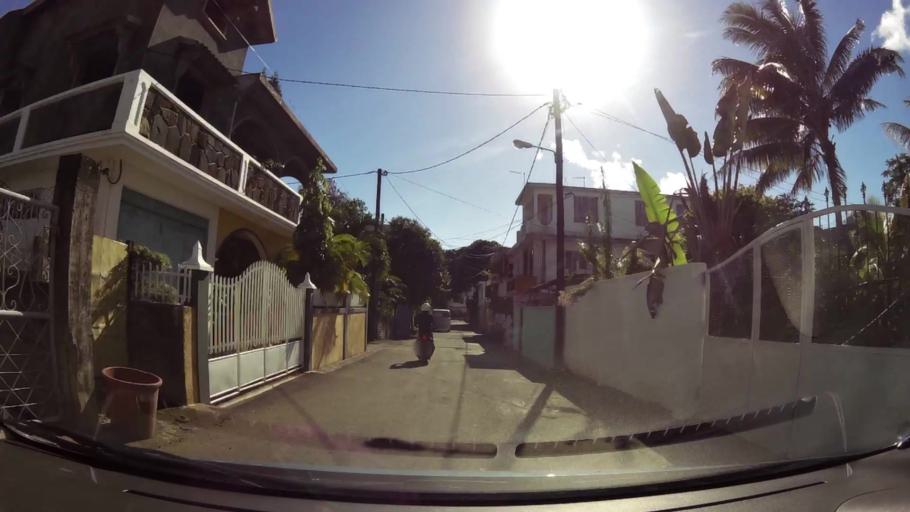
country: MU
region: Grand Port
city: Mahebourg
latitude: -20.4124
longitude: 57.7074
